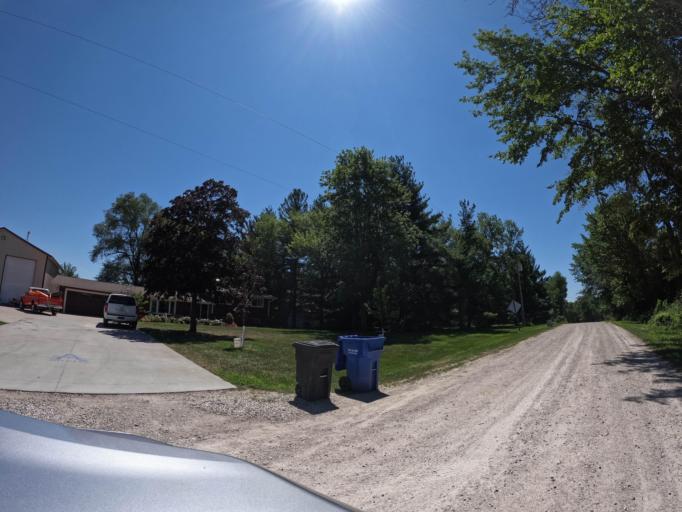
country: US
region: Iowa
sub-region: Monroe County
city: Albia
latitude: 41.0280
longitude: -92.7690
